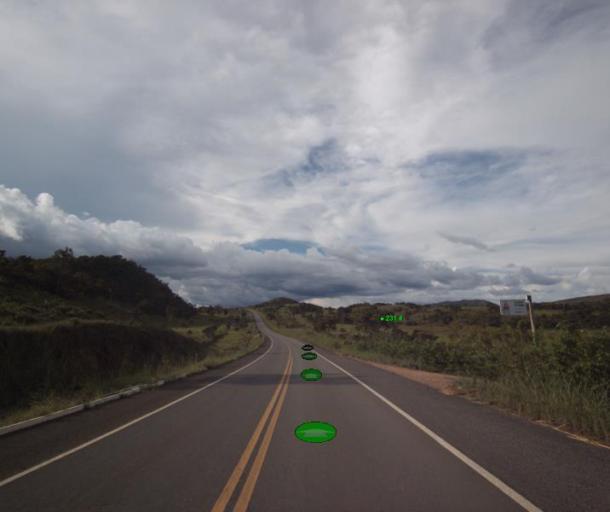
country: BR
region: Goias
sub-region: Niquelandia
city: Niquelandia
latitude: -14.6678
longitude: -48.5890
